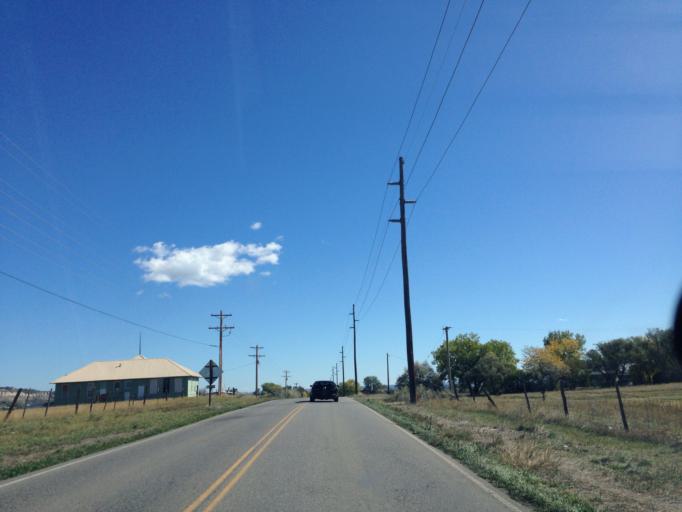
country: US
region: Montana
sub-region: Yellowstone County
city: Laurel
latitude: 45.7840
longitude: -108.6783
